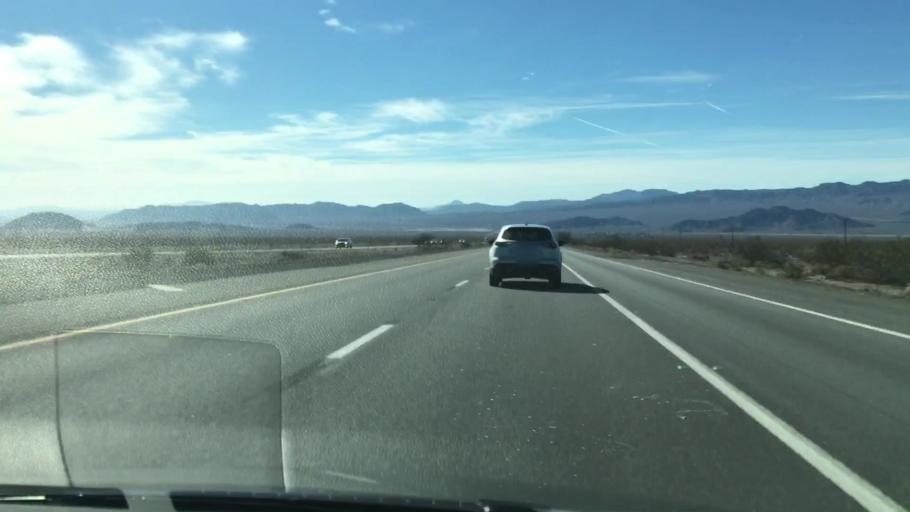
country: US
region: Nevada
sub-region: Clark County
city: Sandy Valley
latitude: 35.3117
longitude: -116.0023
